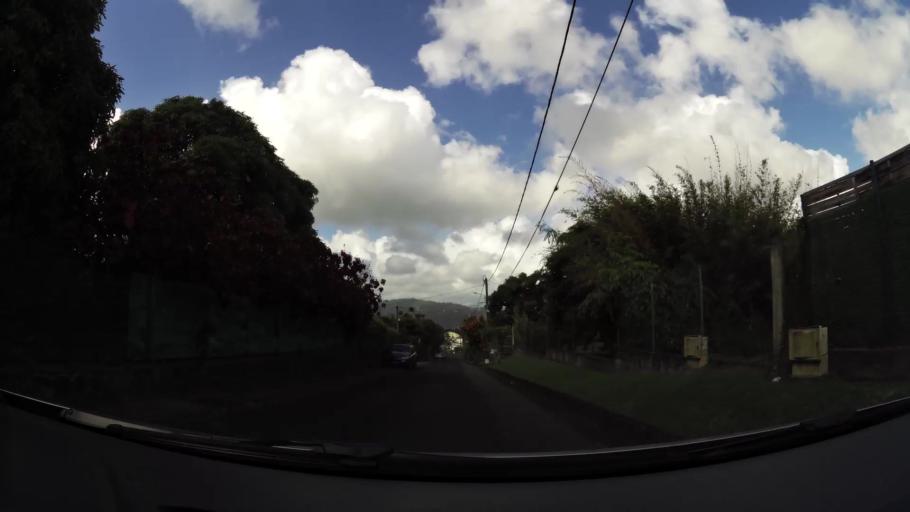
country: MQ
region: Martinique
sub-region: Martinique
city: Saint-Joseph
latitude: 14.6421
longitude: -61.0548
